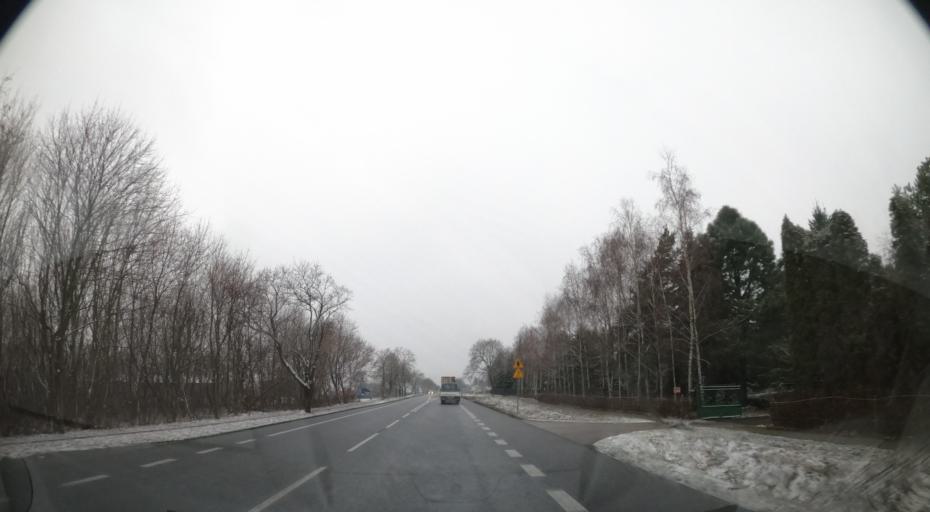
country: PL
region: Masovian Voivodeship
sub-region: Powiat sochaczewski
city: Paprotnia
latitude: 52.2092
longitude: 20.4603
